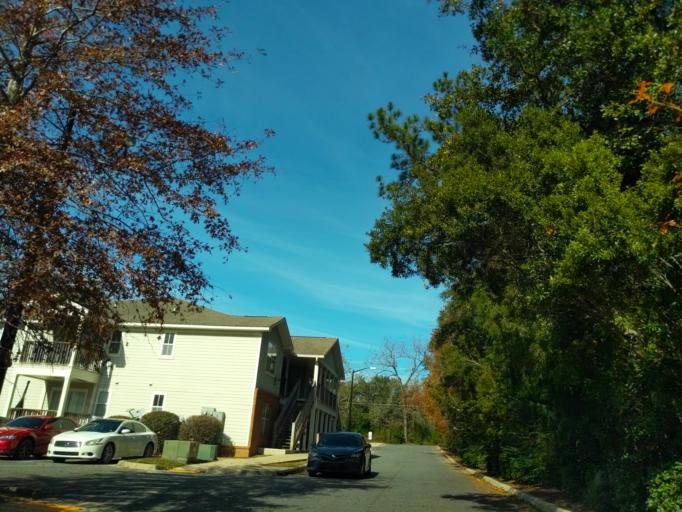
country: US
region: Florida
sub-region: Leon County
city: Tallahassee
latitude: 30.4687
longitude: -84.3421
